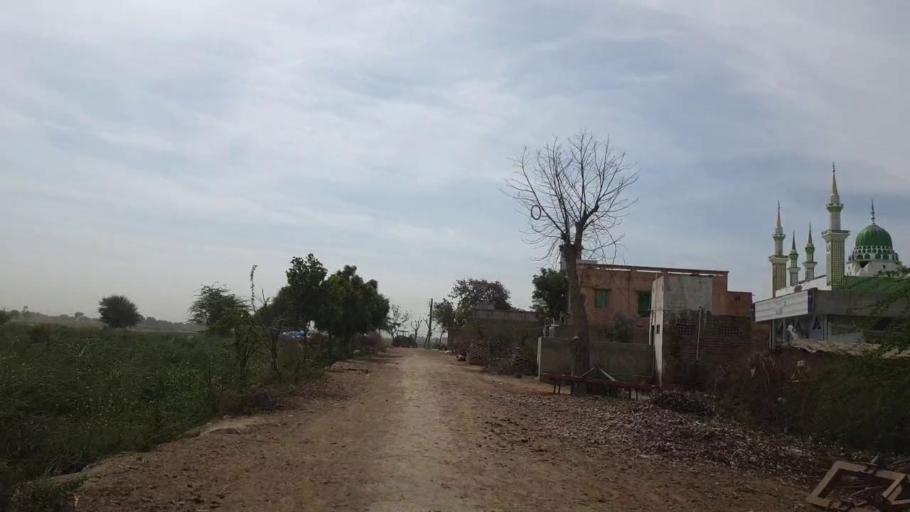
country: PK
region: Sindh
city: Kunri
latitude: 25.1724
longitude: 69.5866
